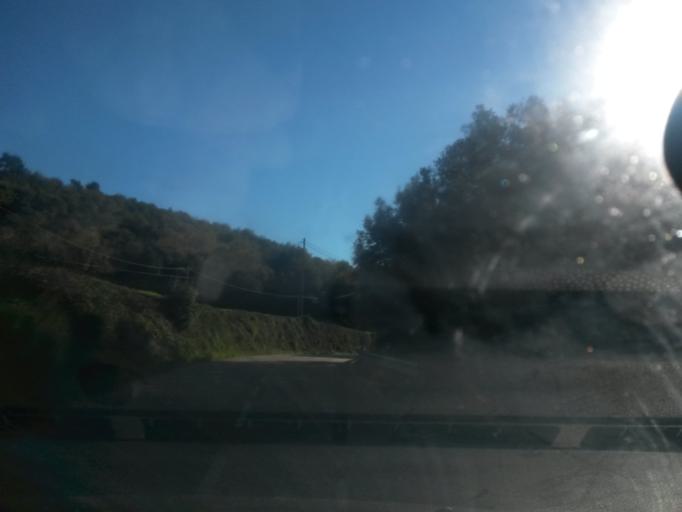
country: ES
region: Catalonia
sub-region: Provincia de Girona
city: la Cellera de Ter
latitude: 41.9689
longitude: 2.6311
